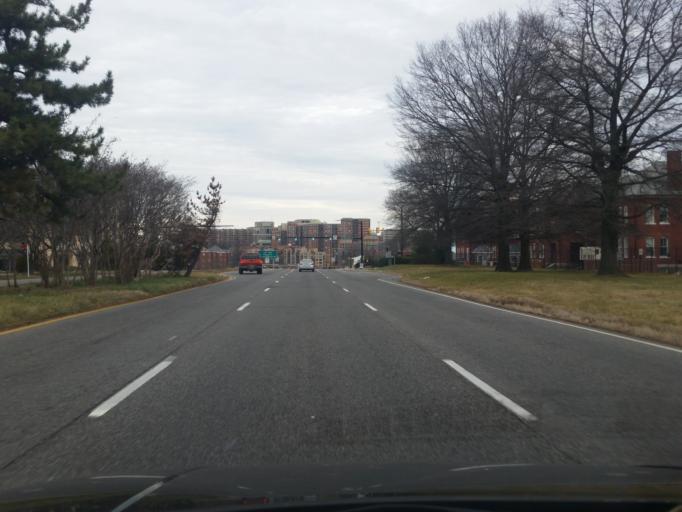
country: US
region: Virginia
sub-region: Arlington County
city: Arlington
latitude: 38.8801
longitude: -77.0839
